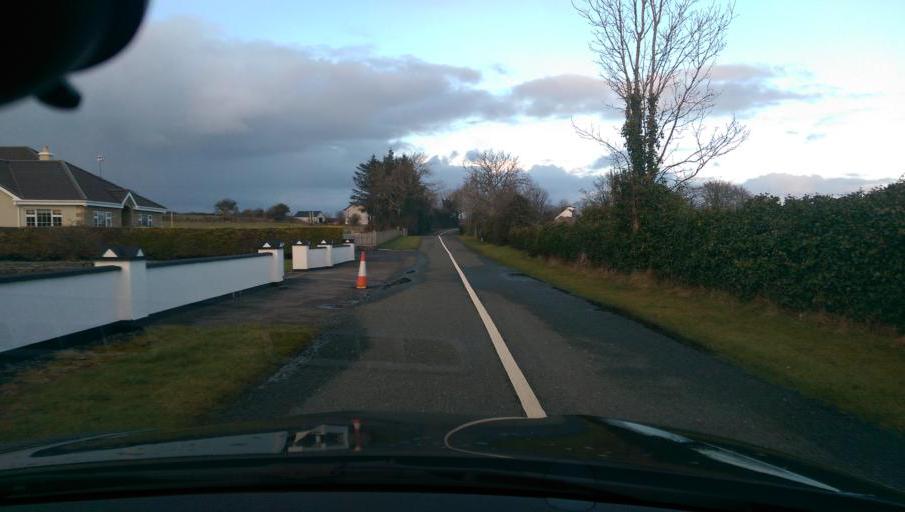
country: IE
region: Connaught
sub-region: County Galway
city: Ballinasloe
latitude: 53.4577
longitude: -8.3806
